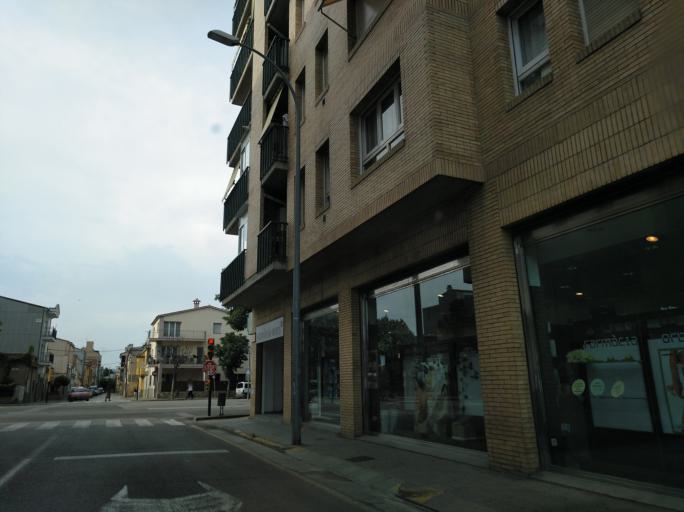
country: ES
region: Catalonia
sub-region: Provincia de Girona
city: Salt
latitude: 41.9732
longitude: 2.7973
